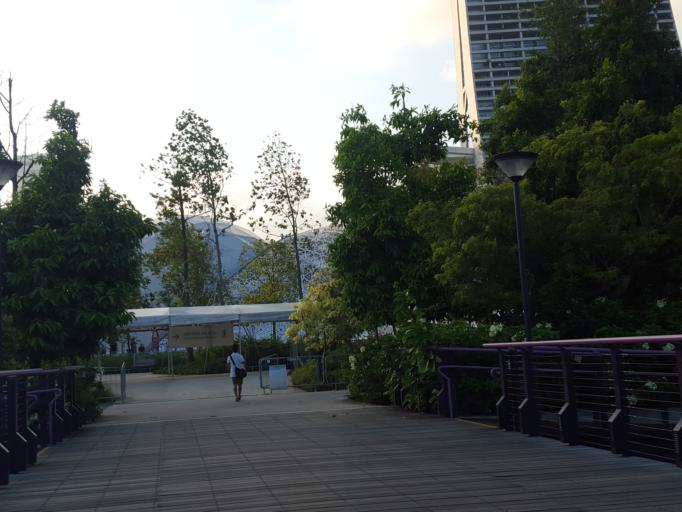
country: SG
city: Singapore
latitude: 1.2807
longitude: 103.8616
